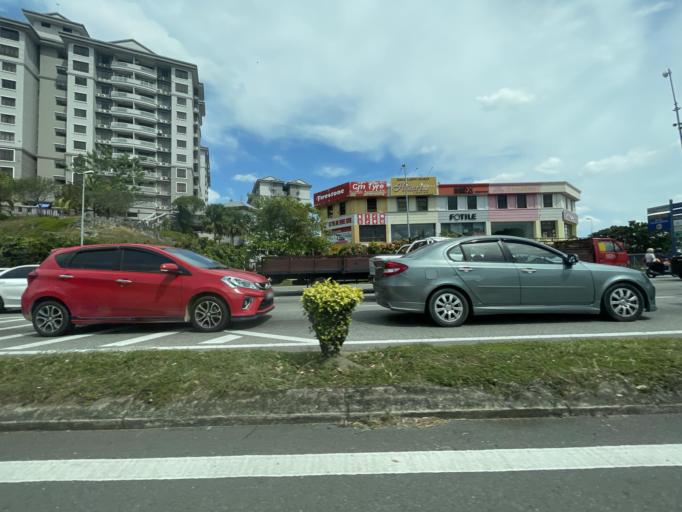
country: MY
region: Melaka
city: Batu Berendam
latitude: 2.2463
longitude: 102.2231
